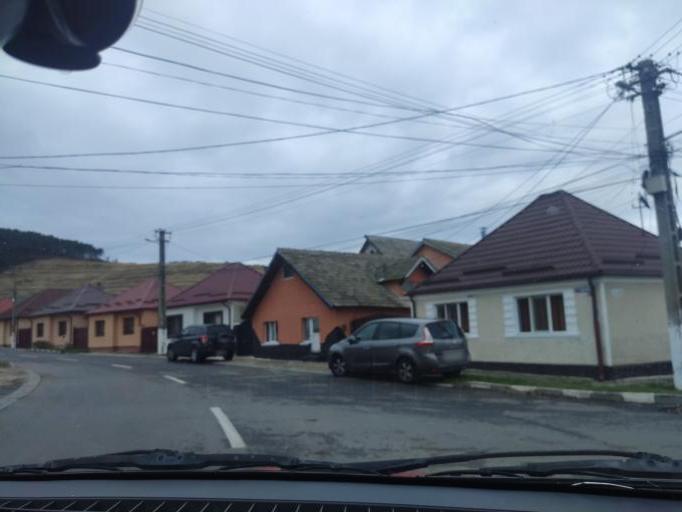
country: RO
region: Brasov
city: Codlea
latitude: 45.7055
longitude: 25.4464
